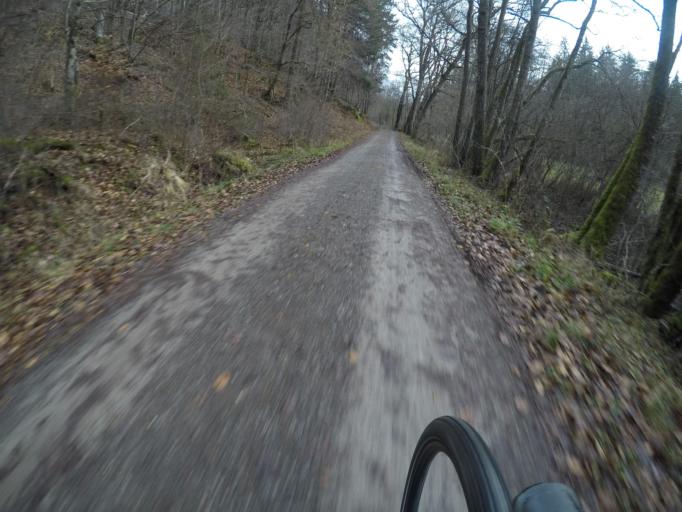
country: DE
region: Baden-Wuerttemberg
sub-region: Regierungsbezirk Stuttgart
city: Waldenbuch
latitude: 48.6054
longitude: 9.1578
